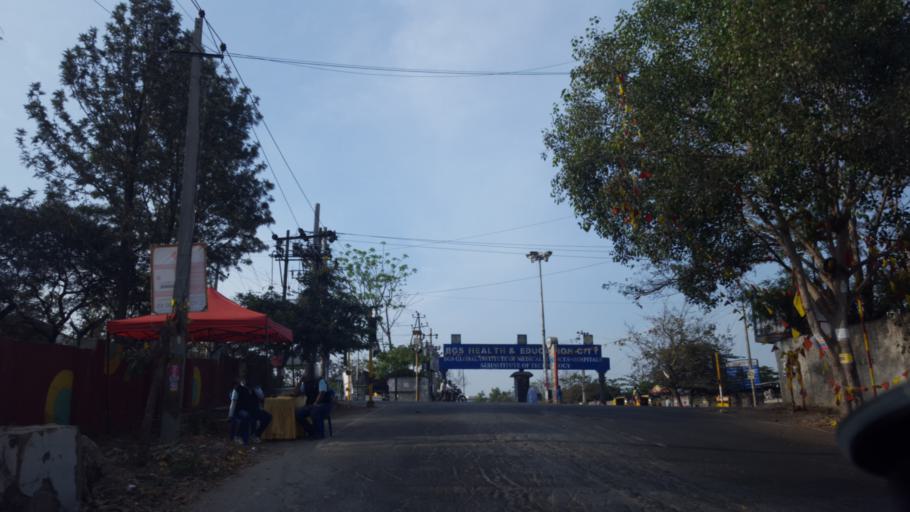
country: IN
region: Karnataka
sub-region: Bangalore Urban
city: Bangalore
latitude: 12.9075
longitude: 77.4993
